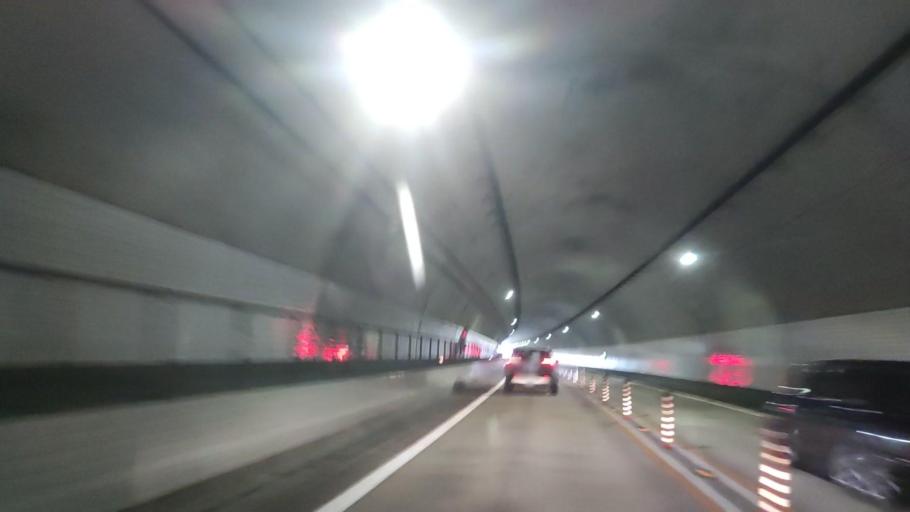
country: JP
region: Kyoto
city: Miyazu
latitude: 35.5547
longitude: 135.1291
